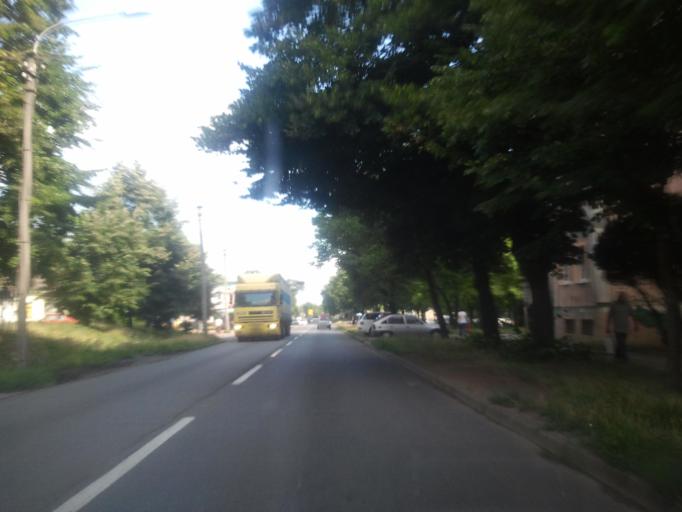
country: RS
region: Autonomna Pokrajina Vojvodina
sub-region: Juznobacki Okrug
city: Petrovaradin
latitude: 45.2382
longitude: 19.8865
